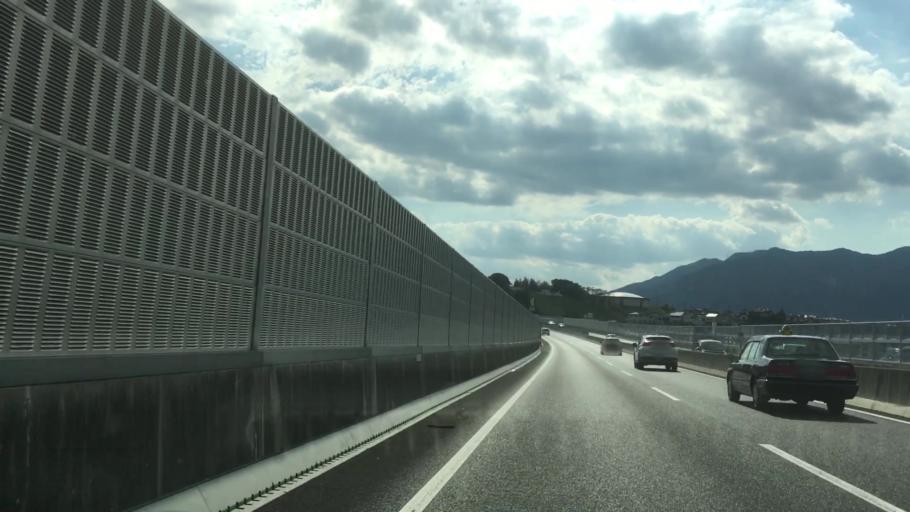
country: JP
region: Hiroshima
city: Hatsukaichi
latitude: 34.3575
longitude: 132.3257
